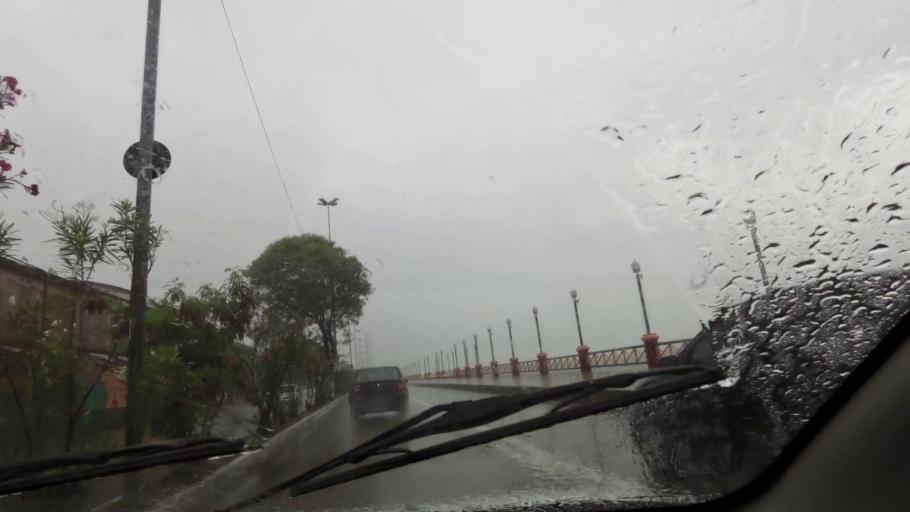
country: BR
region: Pernambuco
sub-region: Recife
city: Recife
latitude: -8.0767
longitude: -34.8898
